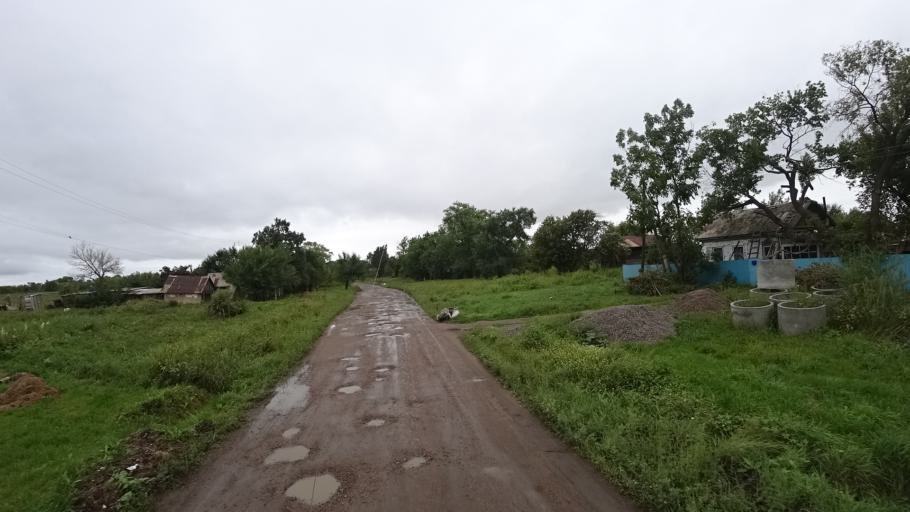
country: RU
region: Primorskiy
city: Chernigovka
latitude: 44.3404
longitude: 132.5477
